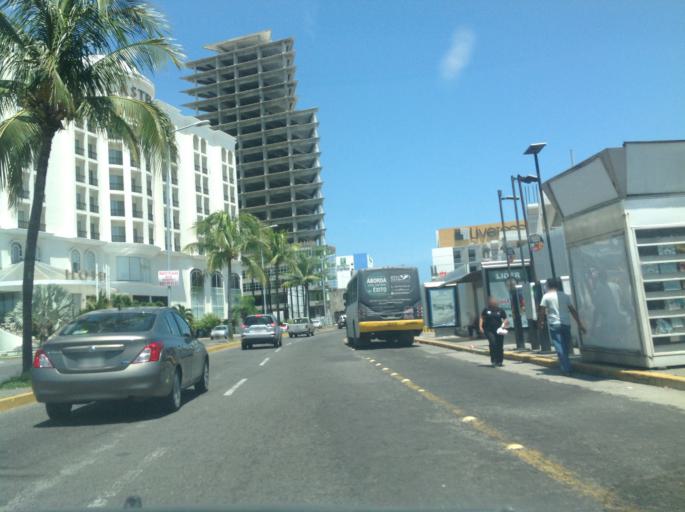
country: MX
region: Veracruz
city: Boca del Rio
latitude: 19.1407
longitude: -96.1068
